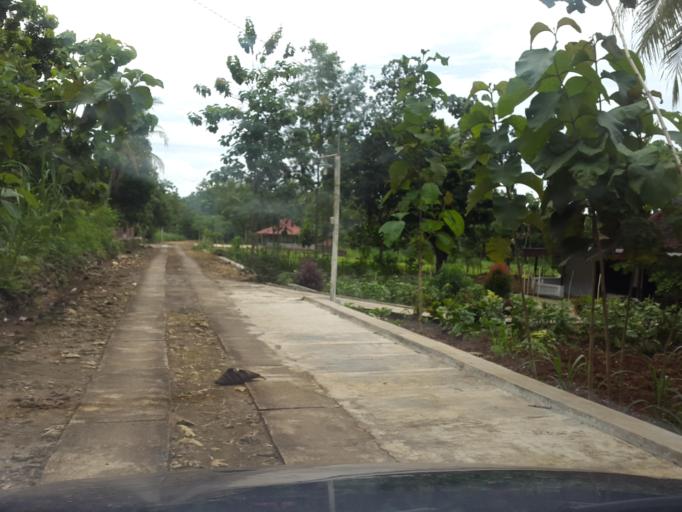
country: ID
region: Daerah Istimewa Yogyakarta
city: Wonosari
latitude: -7.9275
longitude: 110.6771
